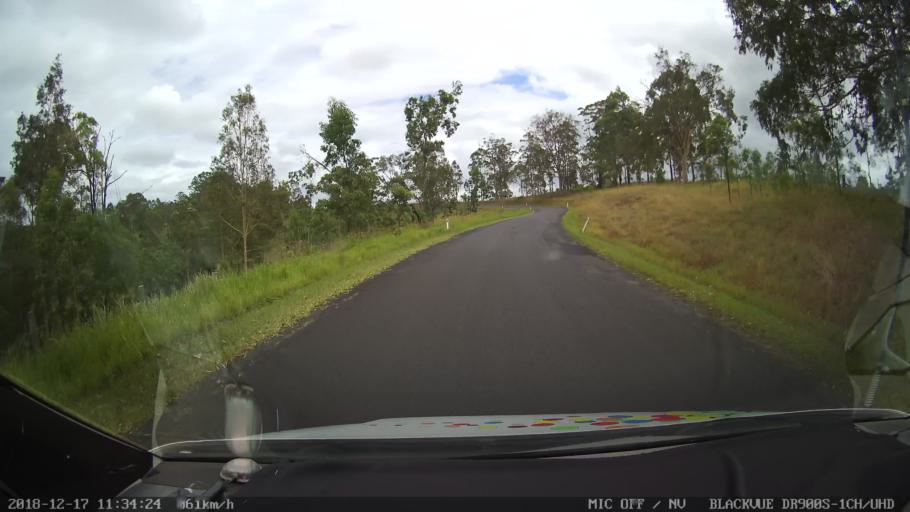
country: AU
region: New South Wales
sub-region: Kyogle
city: Kyogle
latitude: -28.7272
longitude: 152.6137
